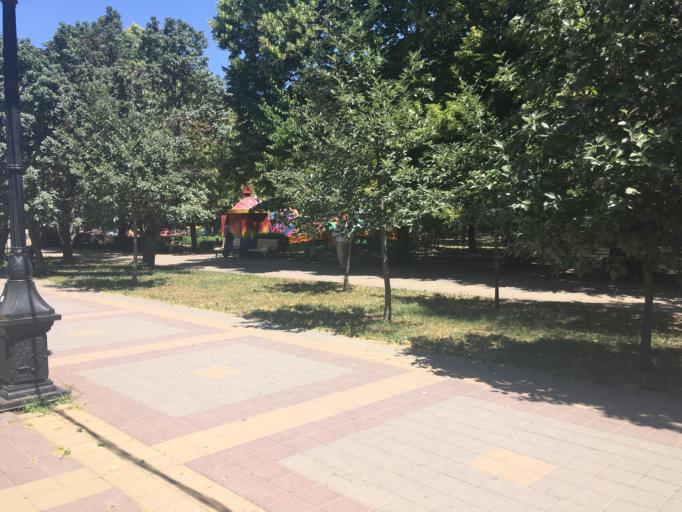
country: RU
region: Rostov
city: Rostov-na-Donu
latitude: 47.2104
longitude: 39.6336
